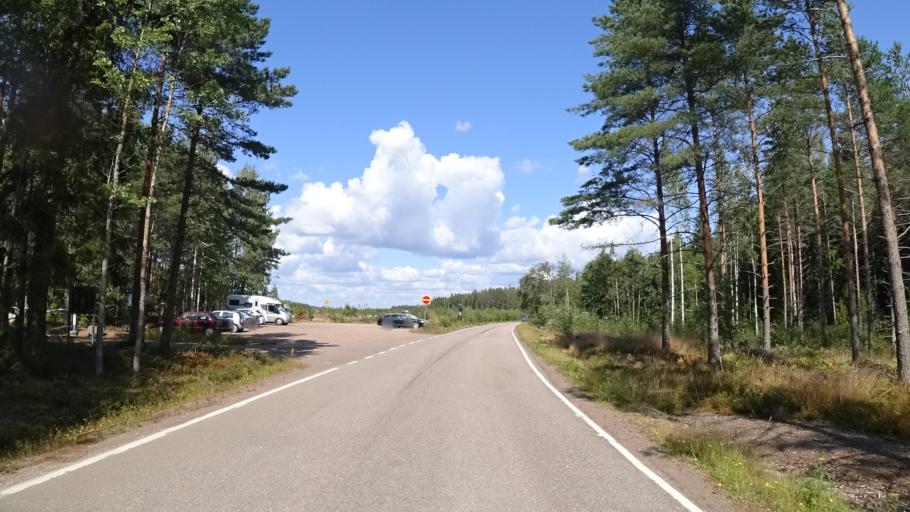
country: FI
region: Kymenlaakso
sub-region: Kotka-Hamina
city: Karhula
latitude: 60.5669
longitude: 26.8988
